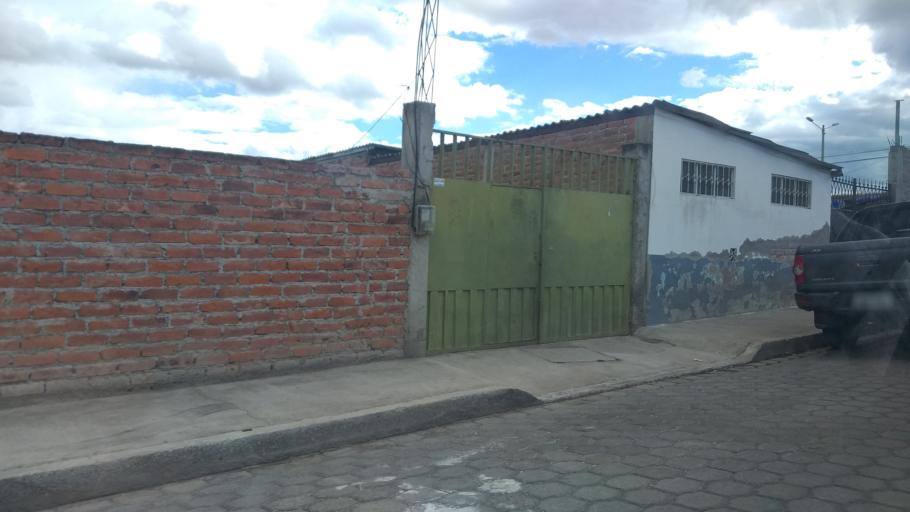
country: EC
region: Chimborazo
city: Riobamba
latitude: -1.6893
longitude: -78.6272
